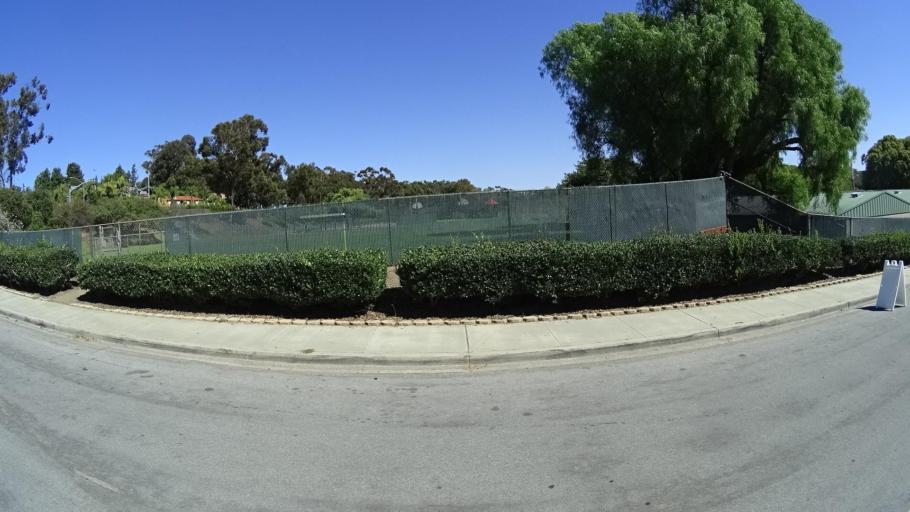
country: US
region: California
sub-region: San Diego County
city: Bonita
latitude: 32.6602
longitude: -117.0491
